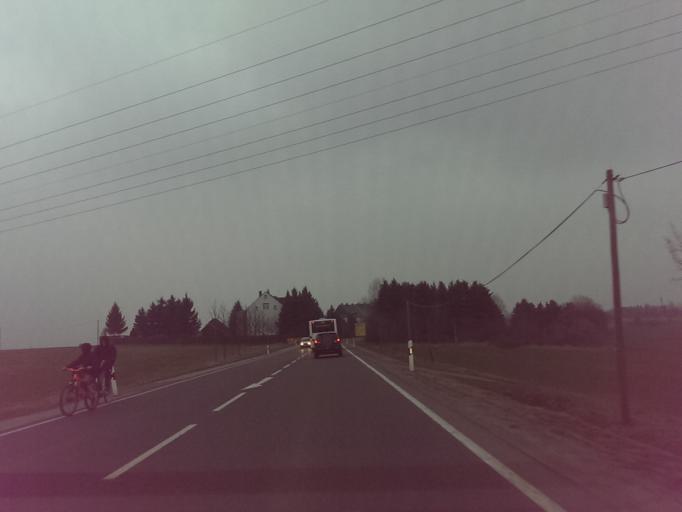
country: DE
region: Saxony
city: Hilbersdorf
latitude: 50.8771
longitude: 12.9796
